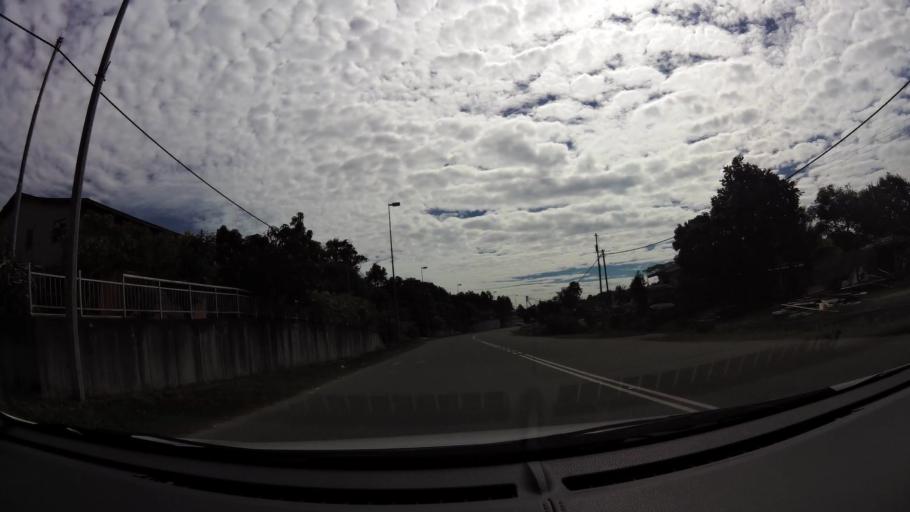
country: BN
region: Brunei and Muara
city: Bandar Seri Begawan
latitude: 4.9125
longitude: 114.9829
